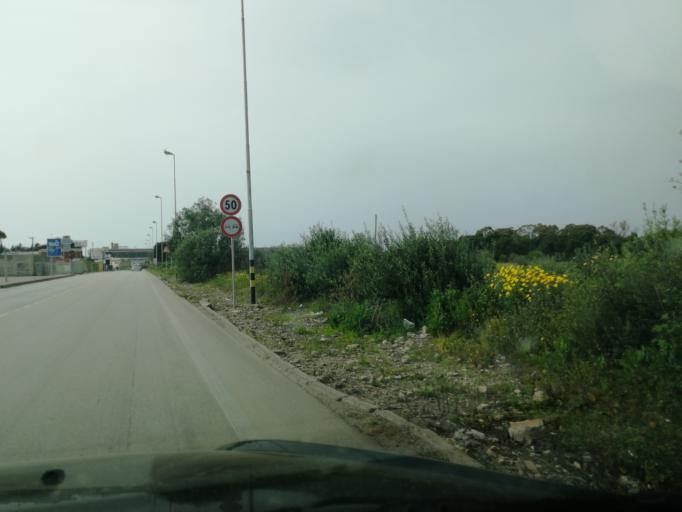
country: IT
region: Apulia
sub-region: Provincia di Barletta - Andria - Trani
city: Barletta
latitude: 41.3138
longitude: 16.3031
